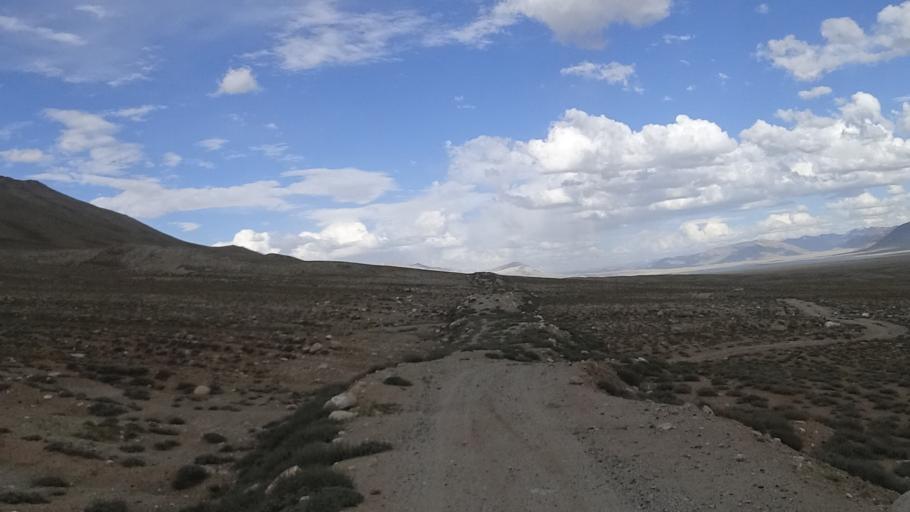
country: TJ
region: Gorno-Badakhshan
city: Murghob
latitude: 37.4686
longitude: 73.5801
